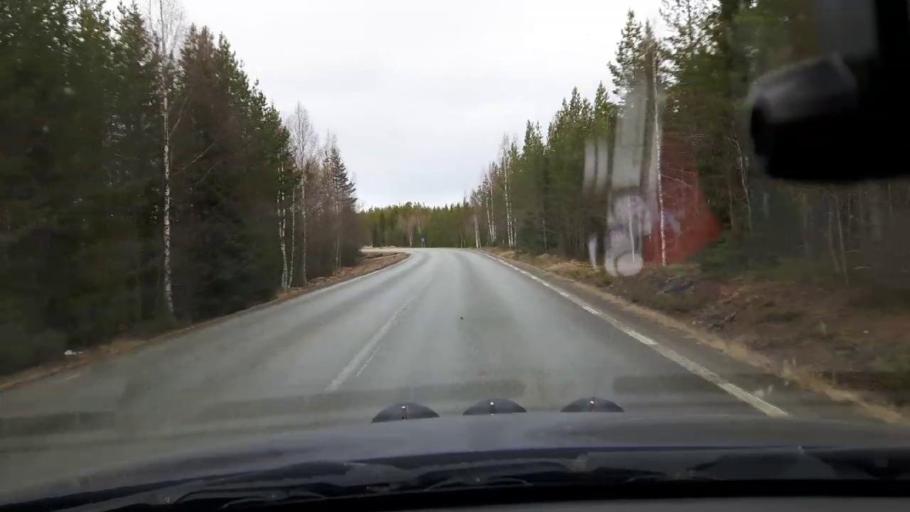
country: SE
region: Jaemtland
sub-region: OEstersunds Kommun
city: Ostersund
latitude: 63.0684
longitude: 14.4476
